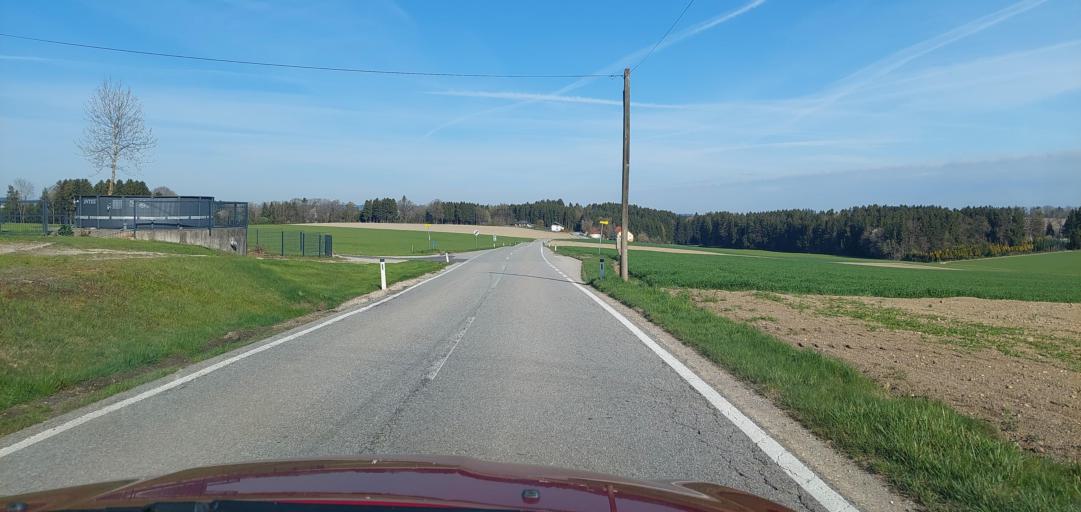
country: AT
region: Upper Austria
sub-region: Politischer Bezirk Ried im Innkreis
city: Ried im Innkreis
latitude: 48.1831
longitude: 13.5175
